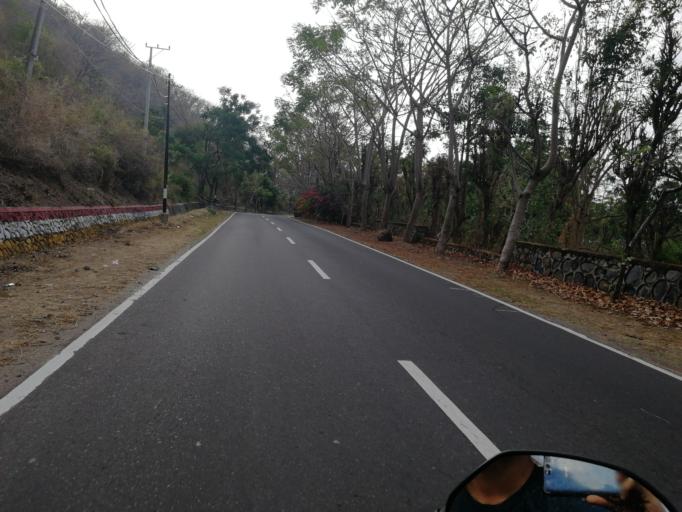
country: ID
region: West Nusa Tenggara
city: Karangsubagan
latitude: -8.4444
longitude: 116.0401
